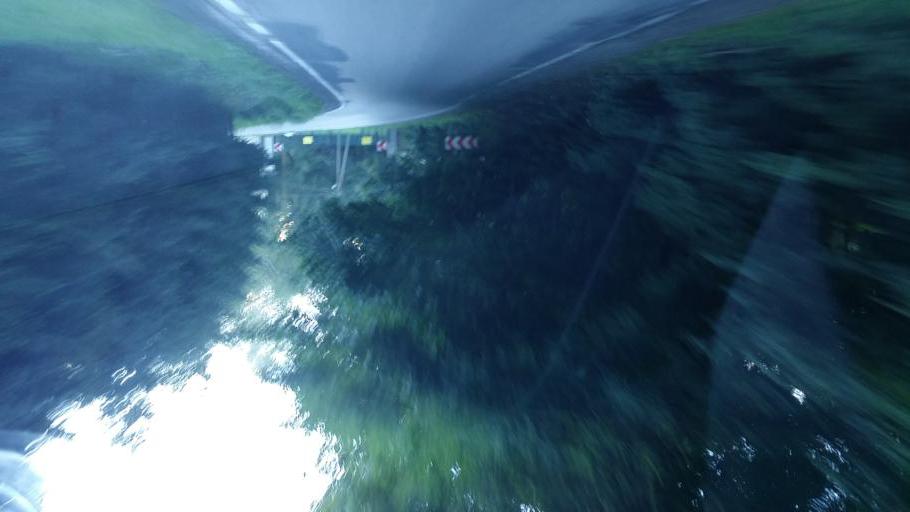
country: PL
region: Lesser Poland Voivodeship
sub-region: Powiat oswiecimski
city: Polanka Wielka
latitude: 49.9884
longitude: 19.3528
